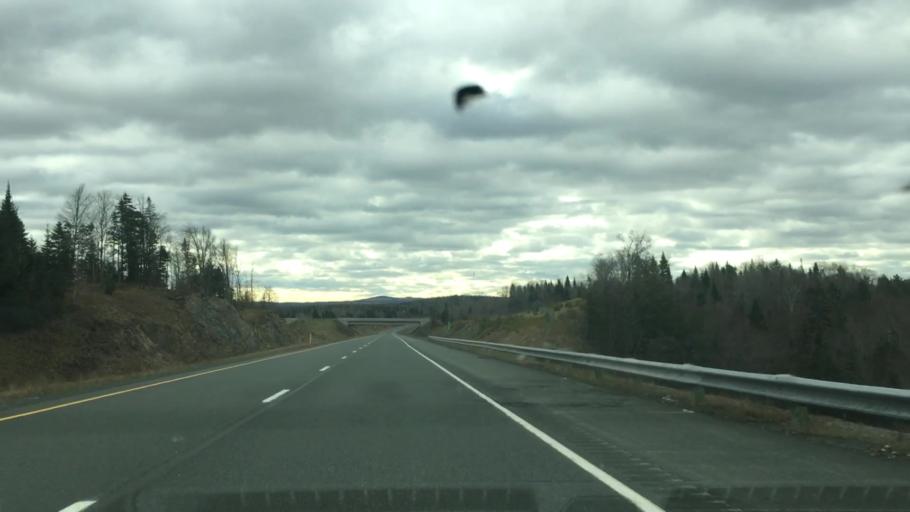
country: US
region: Maine
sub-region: Aroostook County
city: Easton
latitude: 46.6300
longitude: -67.7414
